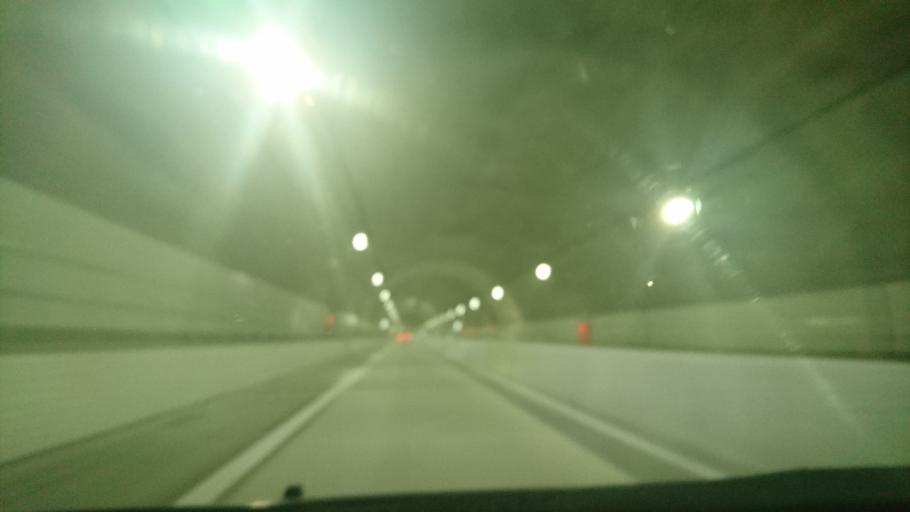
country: JP
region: Iwate
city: Kamaishi
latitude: 39.2322
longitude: 141.8558
